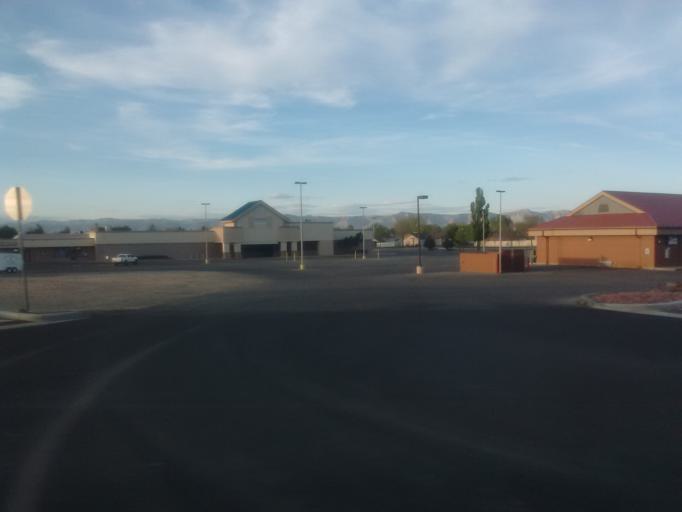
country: US
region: Colorado
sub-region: Mesa County
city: Redlands
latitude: 39.0868
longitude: -108.6513
